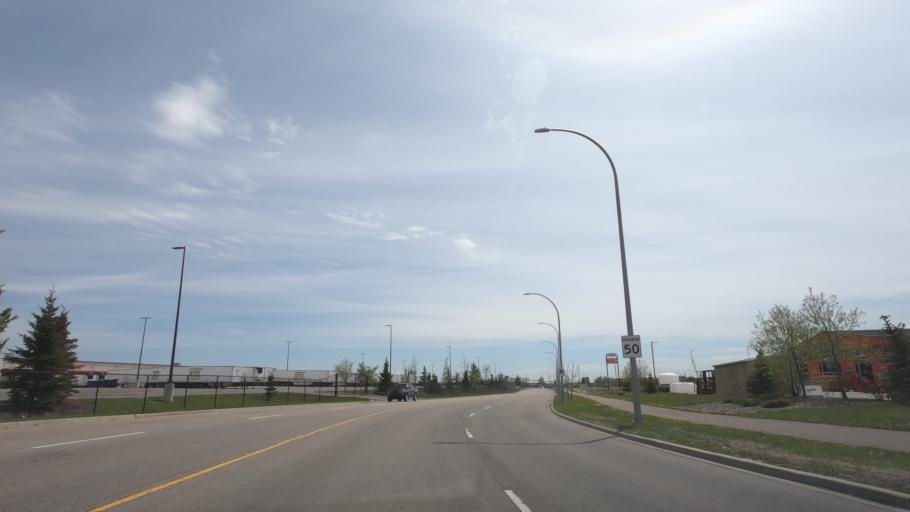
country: CA
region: Alberta
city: Airdrie
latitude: 51.3037
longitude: -113.9950
